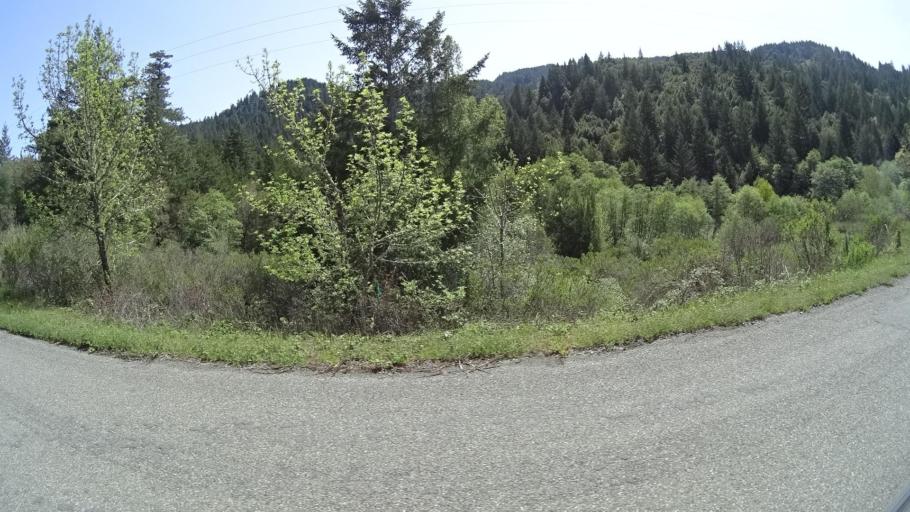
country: US
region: California
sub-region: Humboldt County
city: Redway
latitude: 40.3409
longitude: -123.7043
